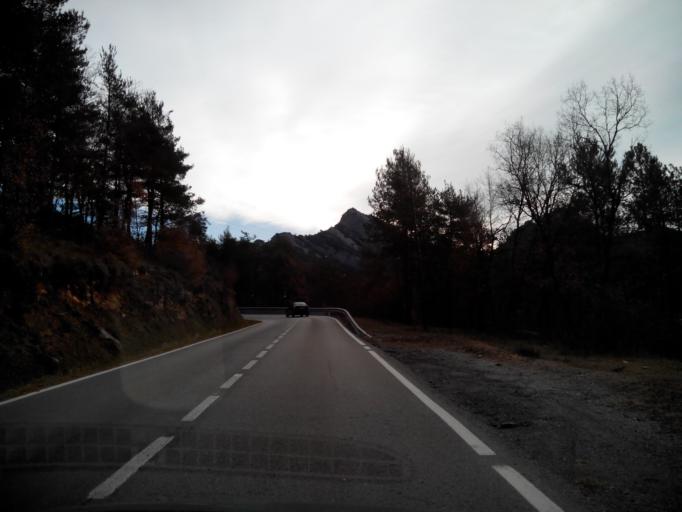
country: ES
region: Catalonia
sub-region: Provincia de Barcelona
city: Vilada
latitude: 42.1343
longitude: 1.9177
